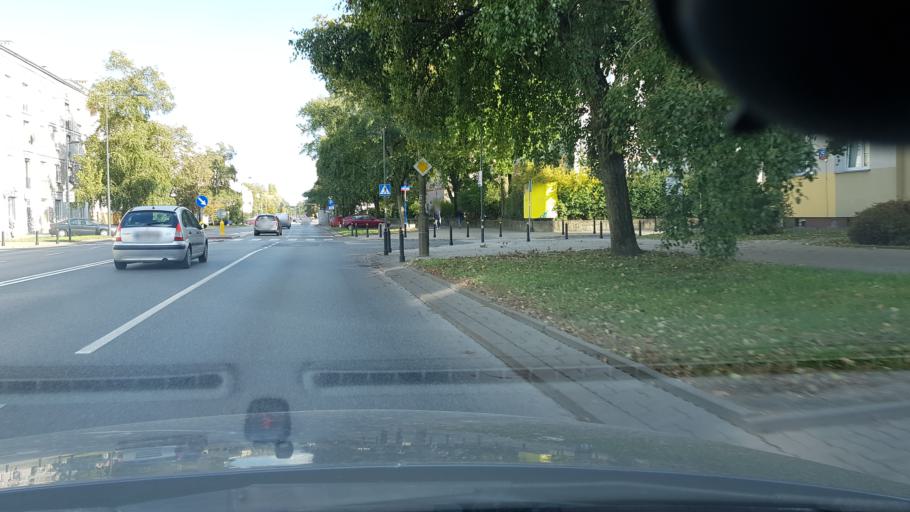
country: PL
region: Masovian Voivodeship
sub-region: Warszawa
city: Bielany
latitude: 52.2767
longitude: 20.9500
